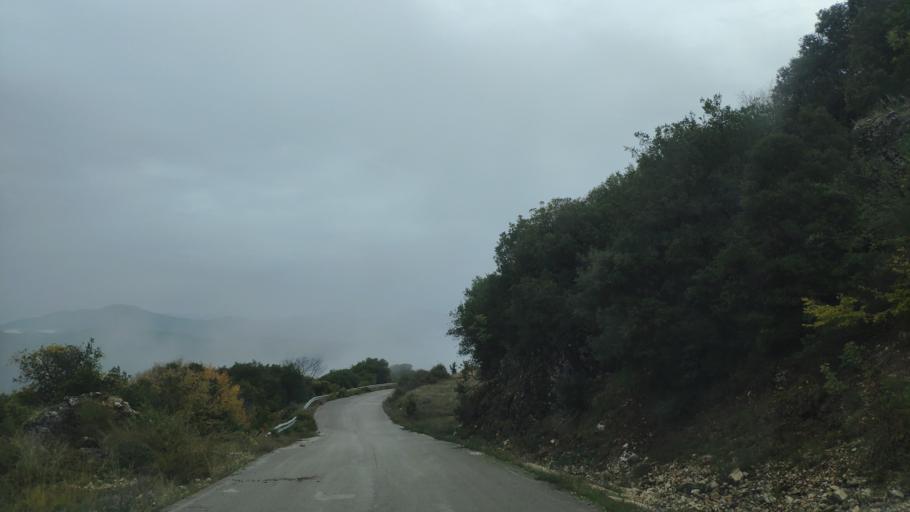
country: GR
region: Epirus
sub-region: Nomos Thesprotias
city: Paramythia
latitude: 39.4582
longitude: 20.6683
